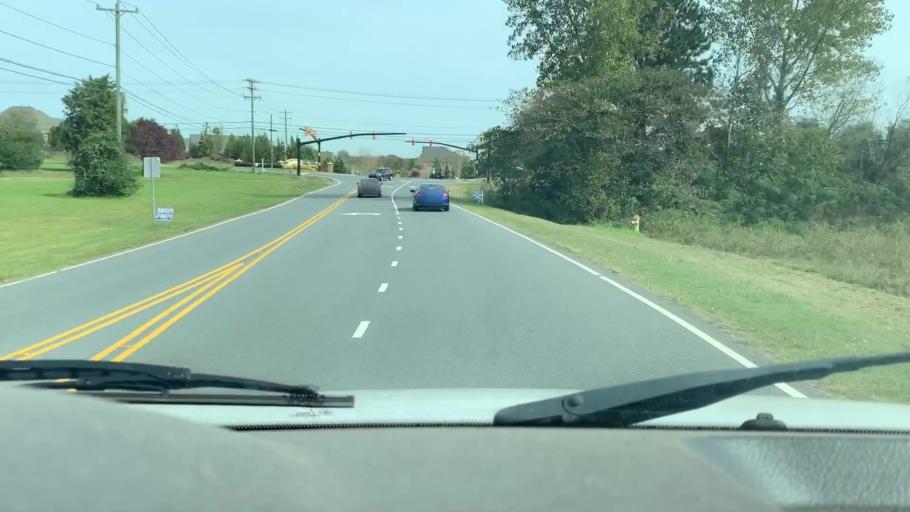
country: US
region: North Carolina
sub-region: Mecklenburg County
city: Huntersville
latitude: 35.4237
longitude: -80.7562
